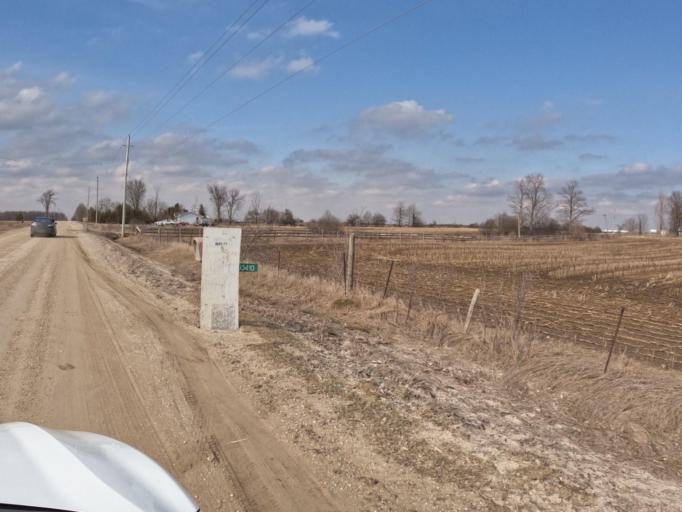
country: CA
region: Ontario
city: Shelburne
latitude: 43.9142
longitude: -80.3045
